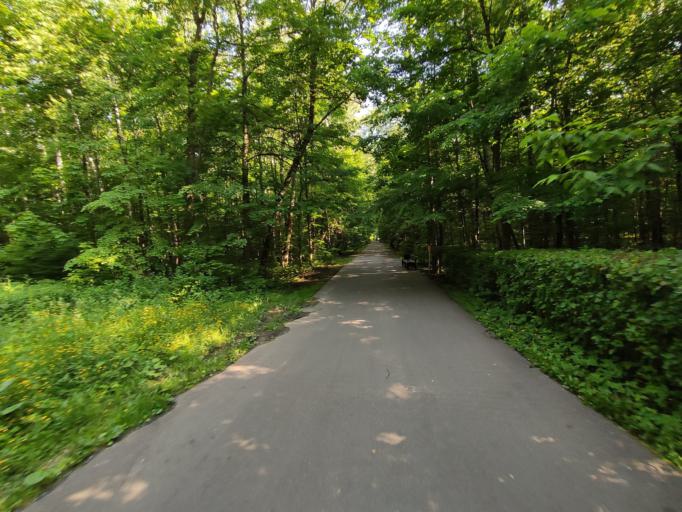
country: RU
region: Moscow
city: Ryazanskiy
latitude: 55.7776
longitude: 37.7532
